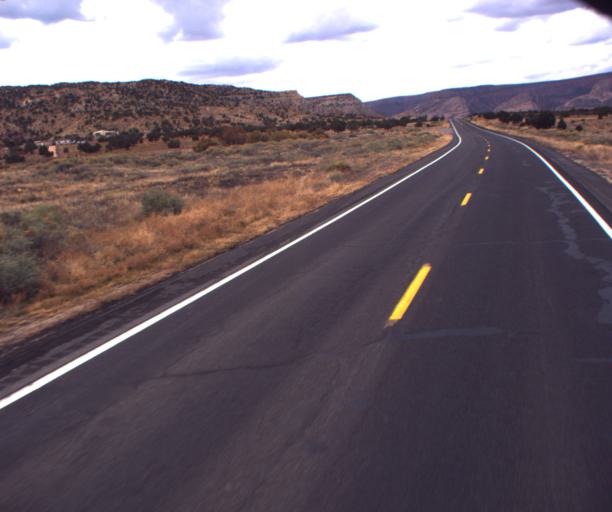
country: US
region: Arizona
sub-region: Navajo County
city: Kayenta
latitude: 36.6985
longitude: -110.3356
